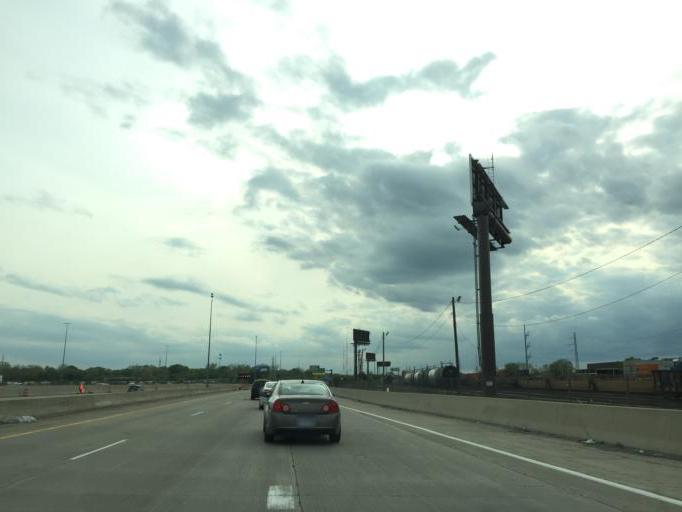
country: US
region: Michigan
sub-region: Wayne County
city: Dearborn Heights
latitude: 42.3786
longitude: -83.2229
